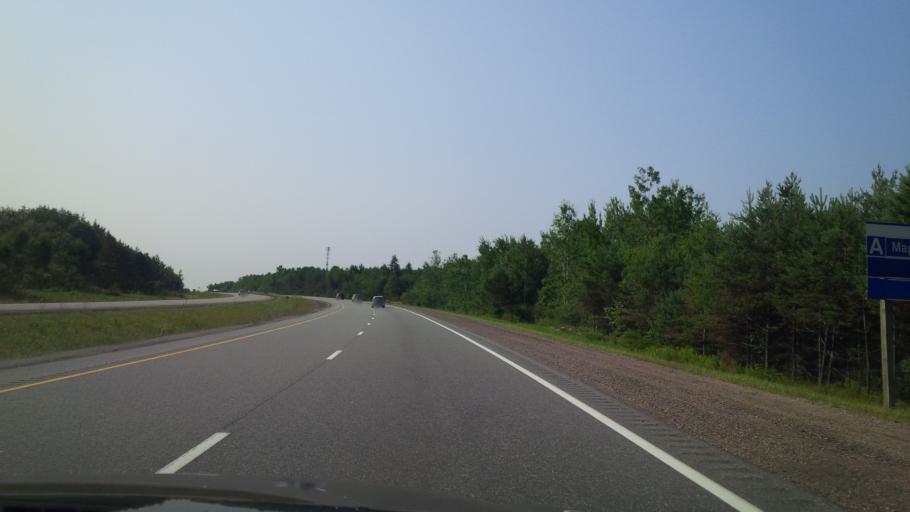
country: CA
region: Ontario
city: Bracebridge
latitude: 45.0633
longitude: -79.2971
